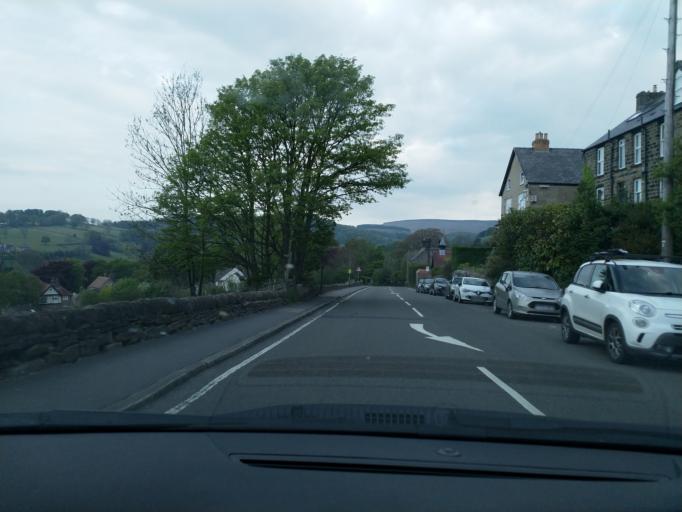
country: GB
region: England
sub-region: Derbyshire
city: Hathersage
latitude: 53.3272
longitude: -1.6491
